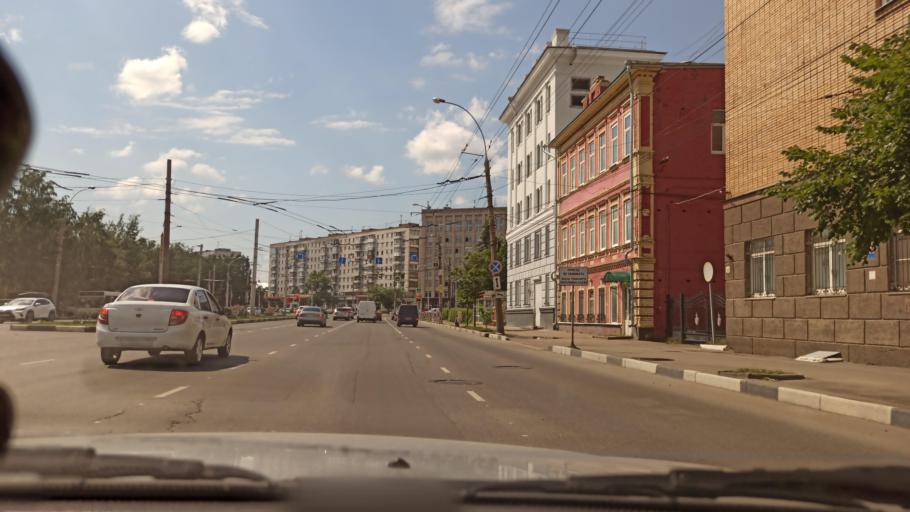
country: RU
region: Vologda
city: Vologda
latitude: 59.2191
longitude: 39.8852
